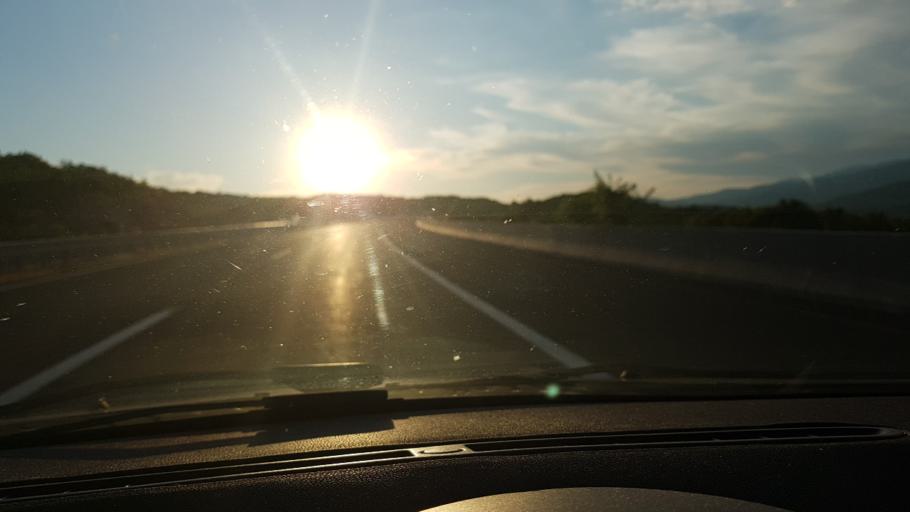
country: HR
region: Splitsko-Dalmatinska
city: Dugopolje
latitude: 43.5826
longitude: 16.6472
